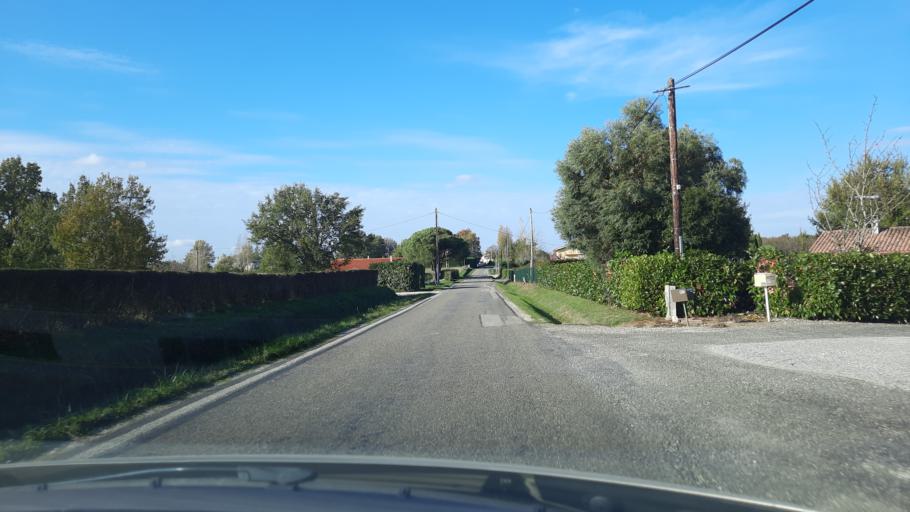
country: FR
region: Midi-Pyrenees
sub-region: Departement du Tarn-et-Garonne
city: Molieres
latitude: 44.1261
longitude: 1.3397
